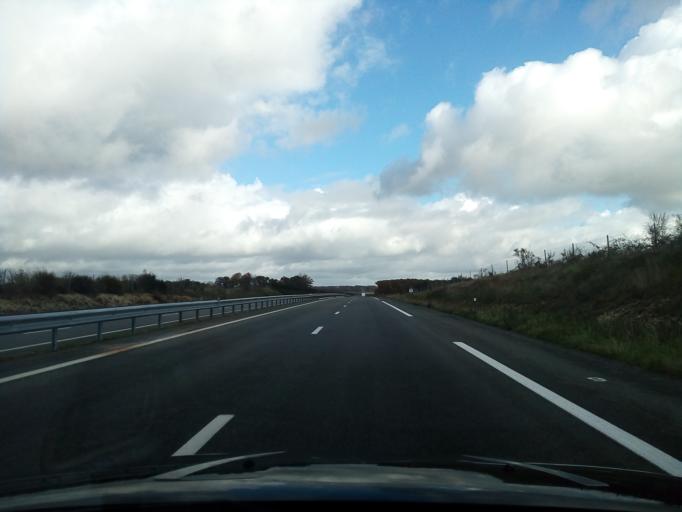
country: FR
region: Limousin
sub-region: Departement de la Creuse
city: Gouzon
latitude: 46.2068
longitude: 2.2703
